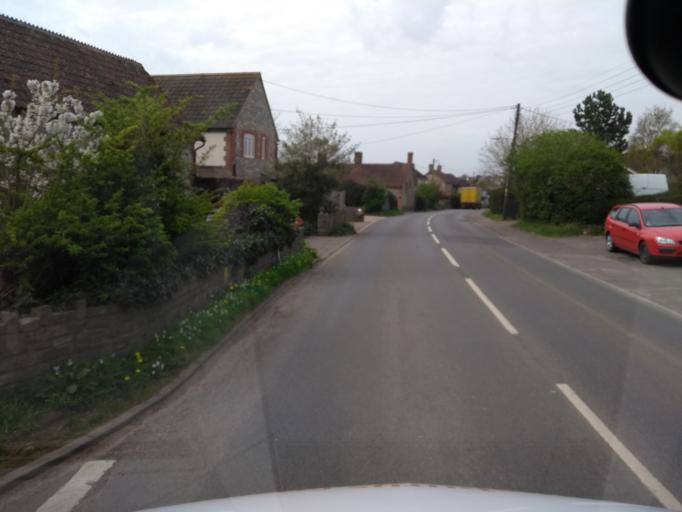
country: GB
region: England
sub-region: Somerset
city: Curry Rivel
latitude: 51.0251
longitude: -2.8592
